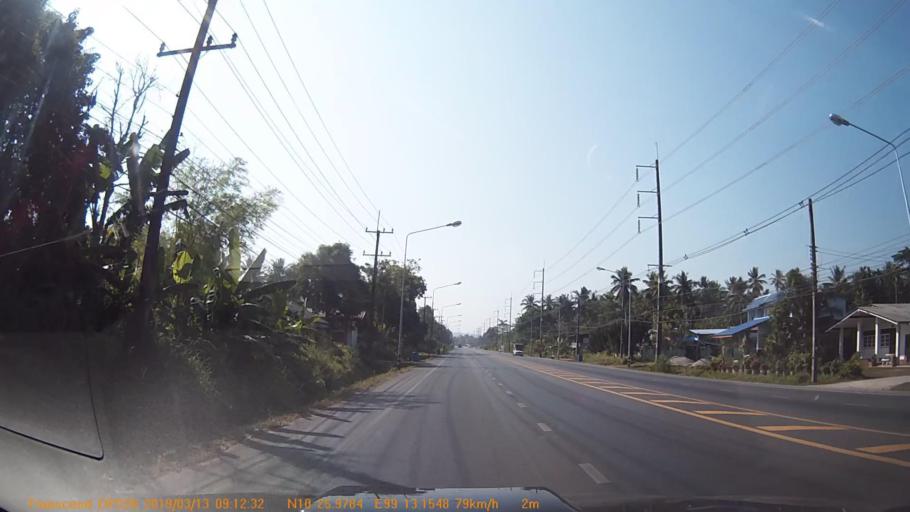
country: TH
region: Chumphon
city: Chumphon
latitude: 10.4327
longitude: 99.2194
